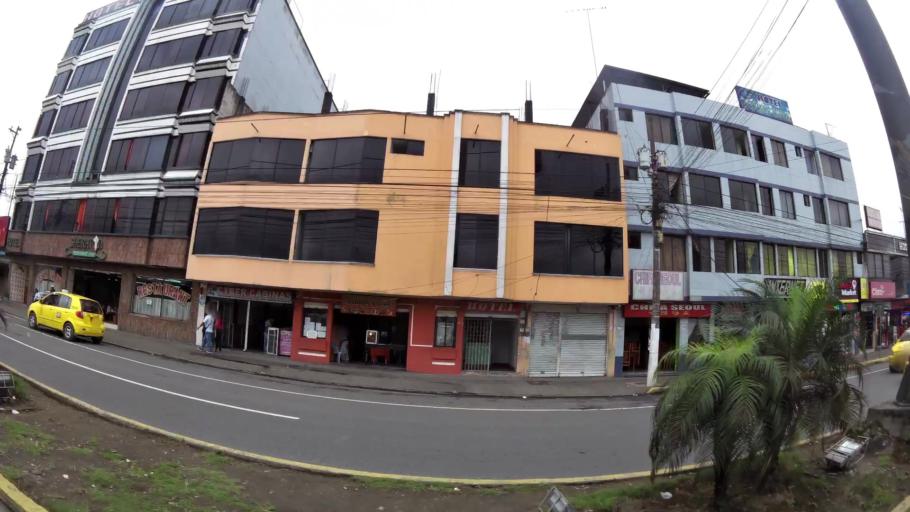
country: EC
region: Santo Domingo de los Tsachilas
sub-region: Canton Santo Domingo de los Colorados
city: Santo Domingo de los Colorados
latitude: -0.2395
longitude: -79.1705
